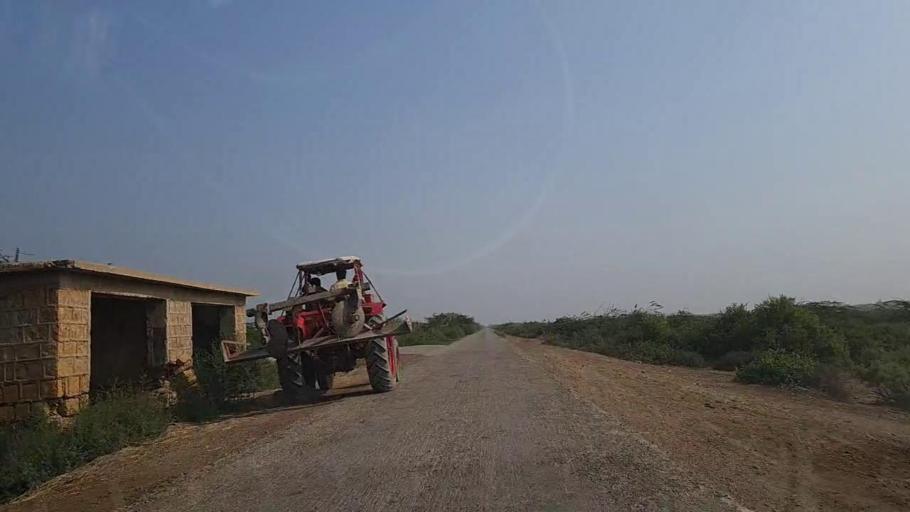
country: PK
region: Sindh
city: Keti Bandar
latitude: 24.2317
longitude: 67.6492
